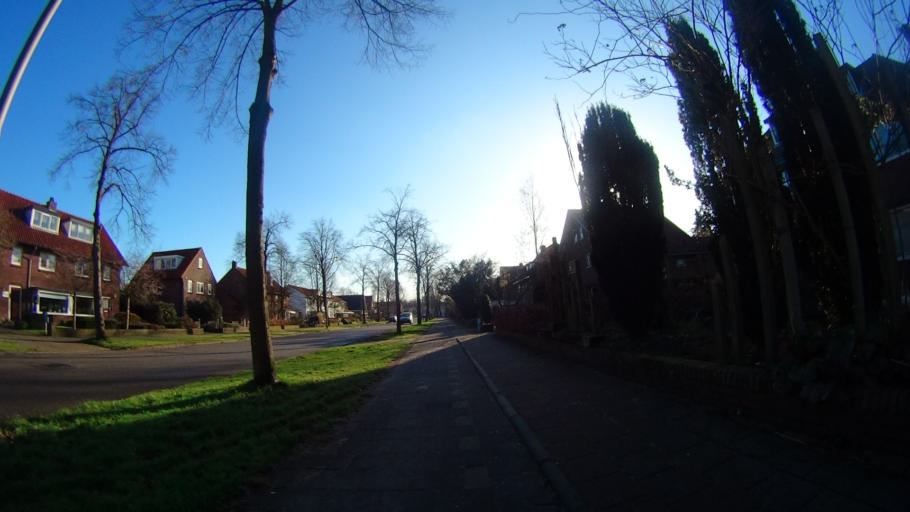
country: NL
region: Utrecht
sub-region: Gemeente Amersfoort
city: Randenbroek
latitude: 52.1542
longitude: 5.4048
